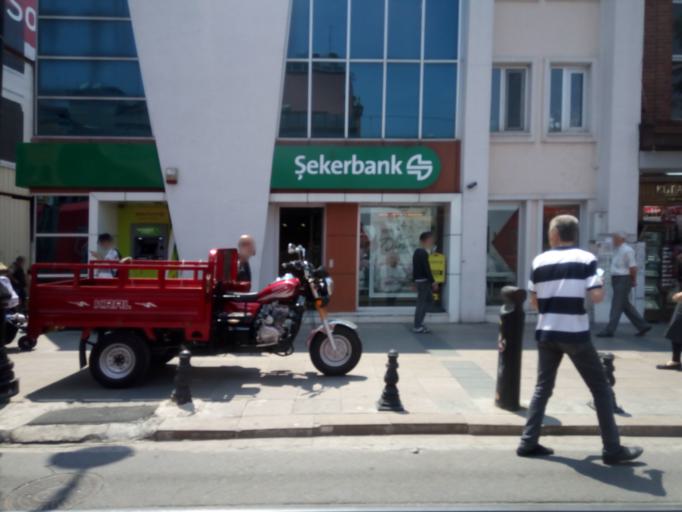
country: TR
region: Istanbul
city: Eminoenue
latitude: 41.0084
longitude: 28.9698
